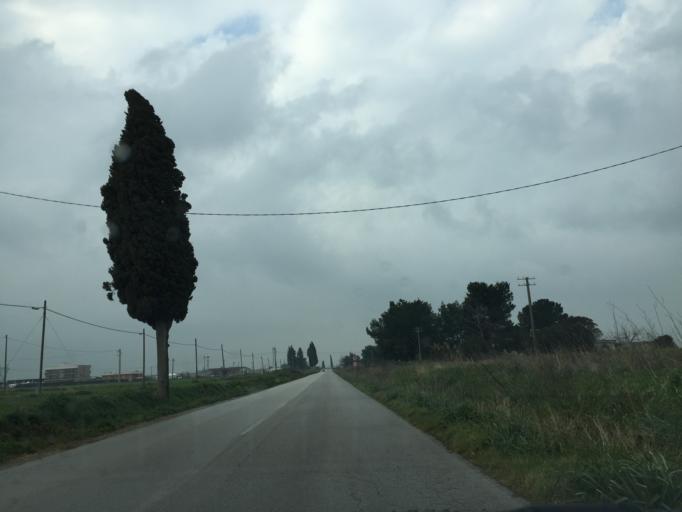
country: IT
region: Apulia
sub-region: Provincia di Foggia
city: Foggia
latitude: 41.4362
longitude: 15.4844
